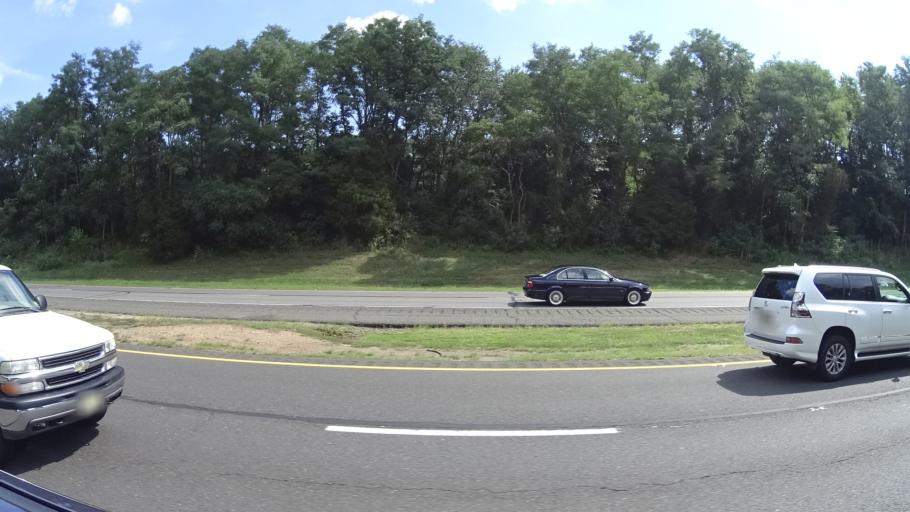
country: US
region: New Jersey
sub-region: Monmouth County
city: Tinton Falls
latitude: 40.3126
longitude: -74.0968
